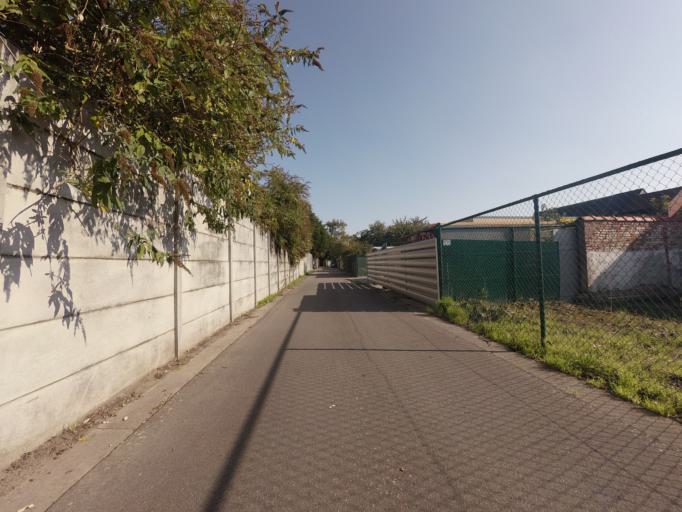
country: BE
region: Flanders
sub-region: Provincie Antwerpen
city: Willebroek
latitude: 51.0709
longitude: 4.3540
